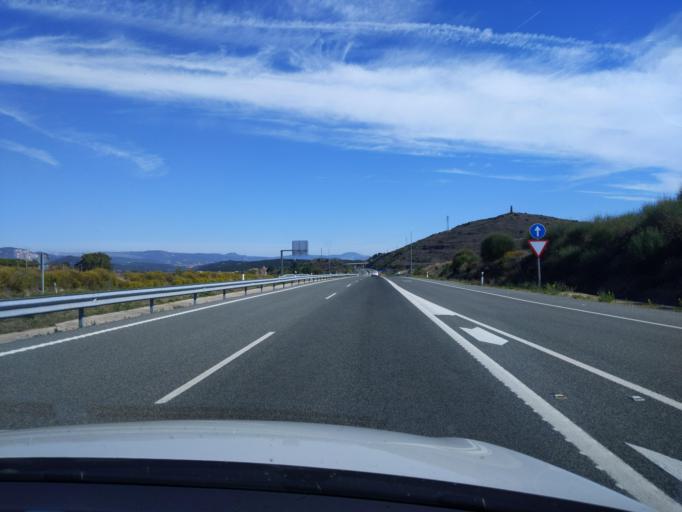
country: ES
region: Navarre
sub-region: Provincia de Navarra
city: Villamayor de Monjardin
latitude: 42.6263
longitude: -2.0953
